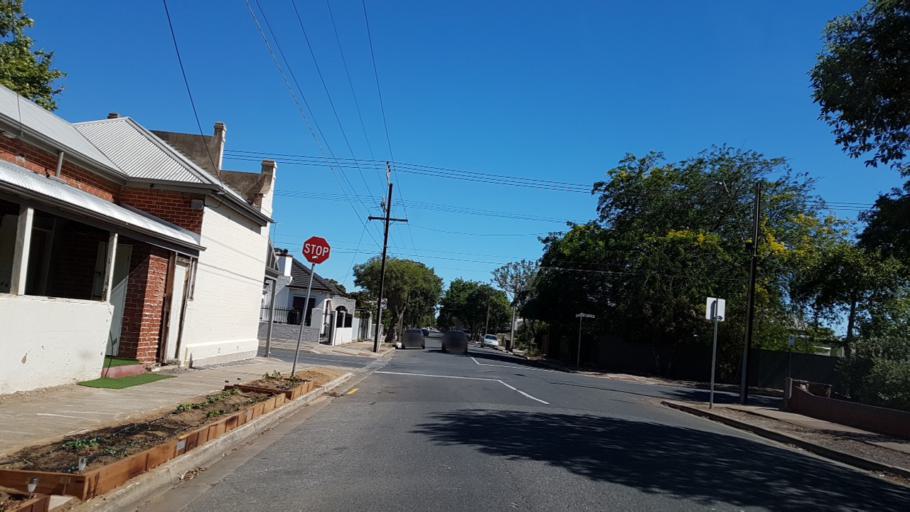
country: AU
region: South Australia
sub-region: City of West Torrens
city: Thebarton
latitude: -34.9180
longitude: 138.5609
